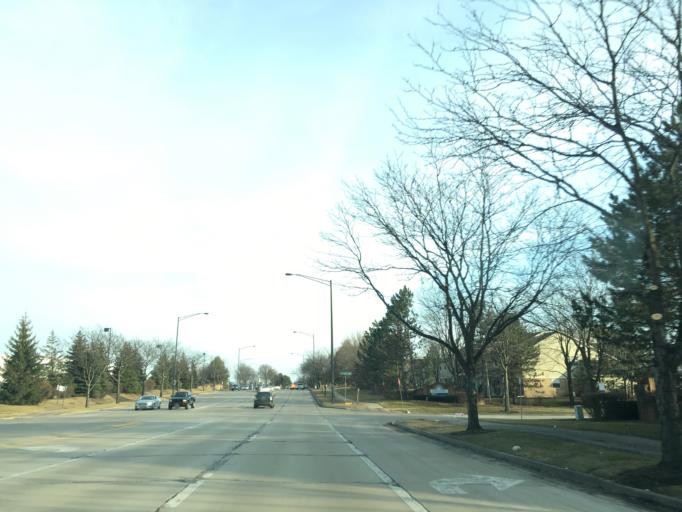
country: US
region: Illinois
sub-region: DuPage County
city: Hanover Park
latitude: 42.0267
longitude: -88.1498
